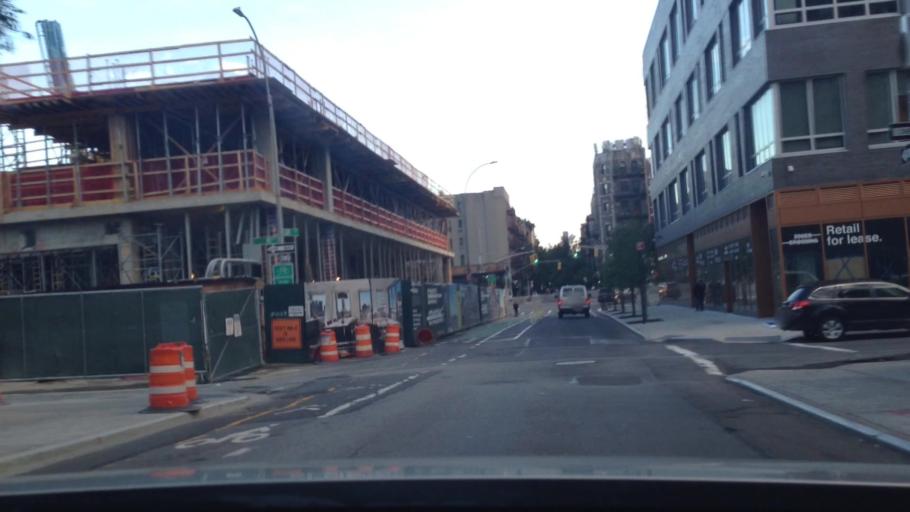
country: US
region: New York
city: New York City
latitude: 40.7167
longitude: -73.9863
